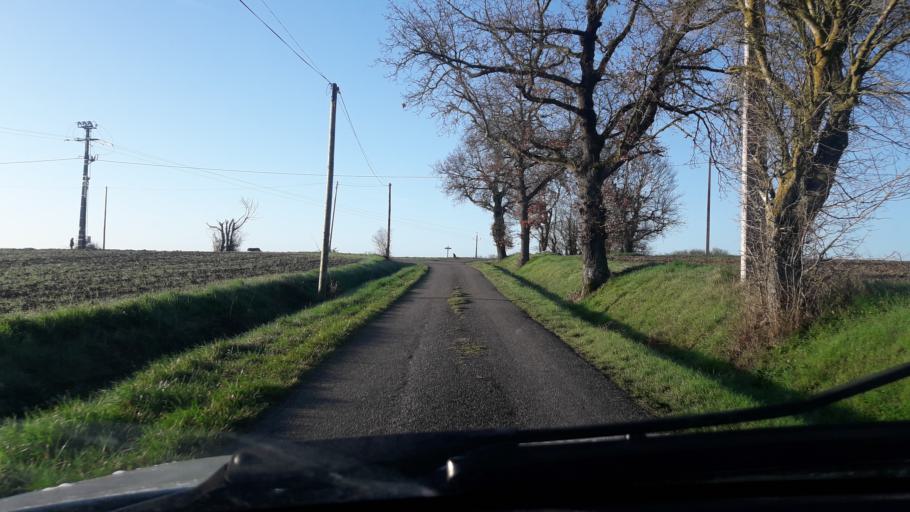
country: FR
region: Midi-Pyrenees
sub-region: Departement du Gers
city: Gimont
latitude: 43.6366
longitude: 0.9918
